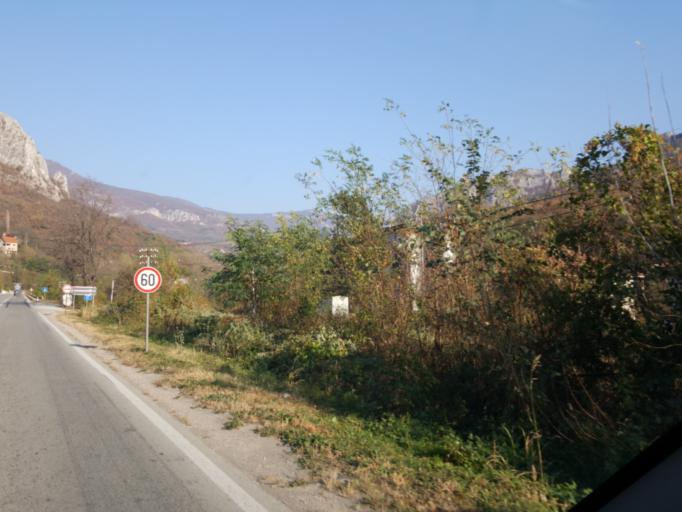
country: RS
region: Central Serbia
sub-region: Nisavski Okrug
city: Niska Banja
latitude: 43.3297
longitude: 22.0635
